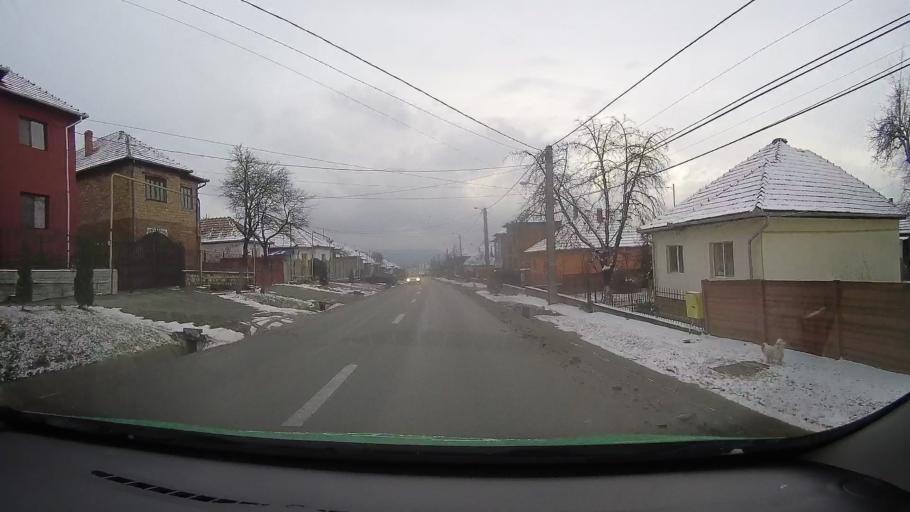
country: RO
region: Hunedoara
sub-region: Oras Hateg
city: Hateg
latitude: 45.6189
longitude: 22.9417
